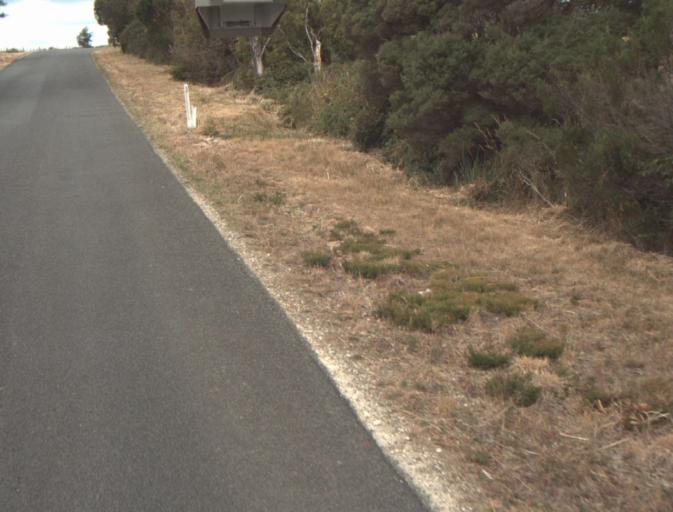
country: AU
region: Tasmania
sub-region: Launceston
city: Mayfield
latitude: -41.2011
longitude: 147.0864
